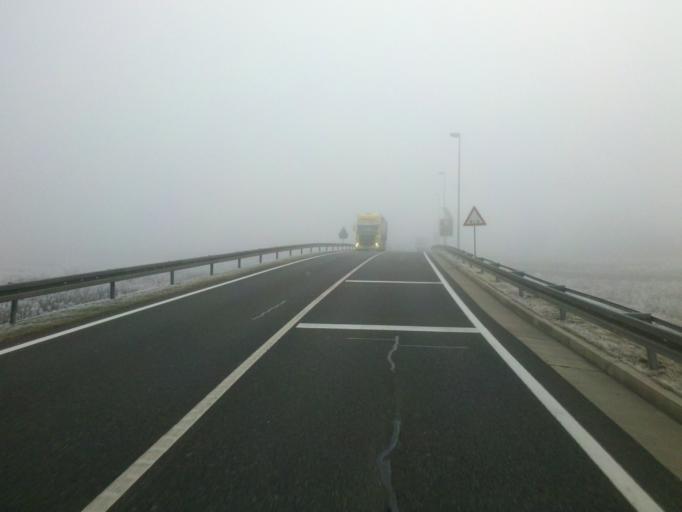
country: HR
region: Varazdinska
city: Jalkovec
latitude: 46.2943
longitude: 16.3039
